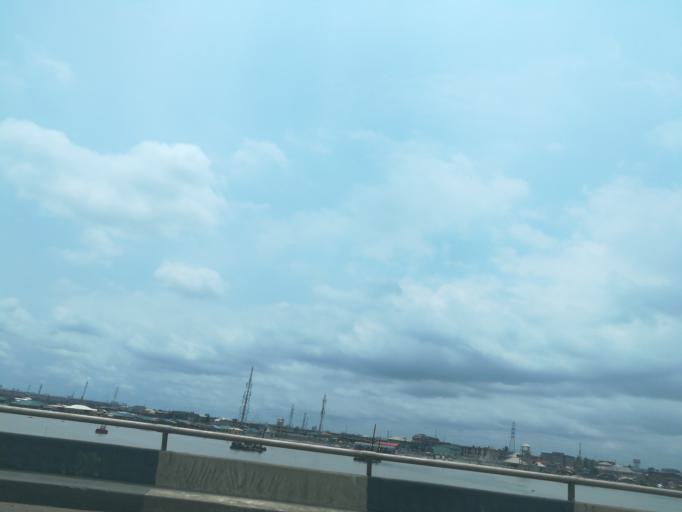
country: NG
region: Lagos
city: Somolu
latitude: 6.5292
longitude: 3.4025
